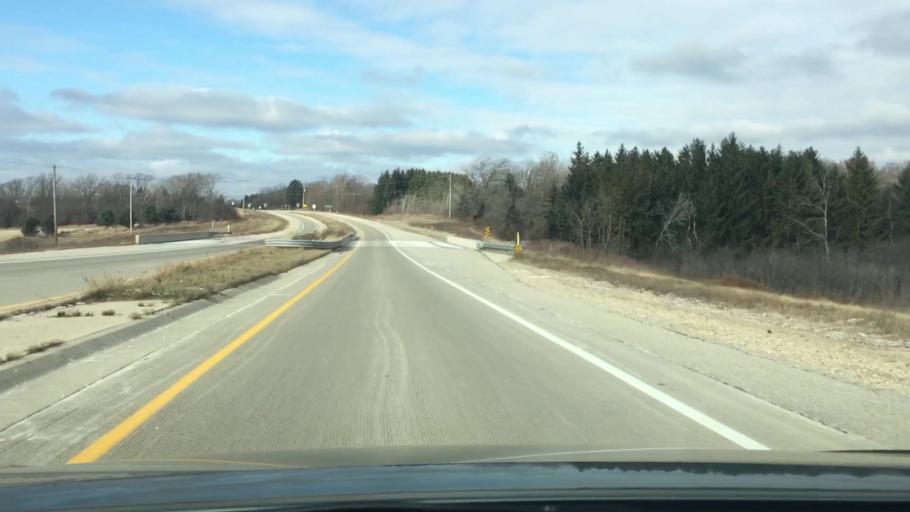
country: US
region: Wisconsin
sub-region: Waukesha County
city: North Prairie
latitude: 42.9427
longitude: -88.3482
